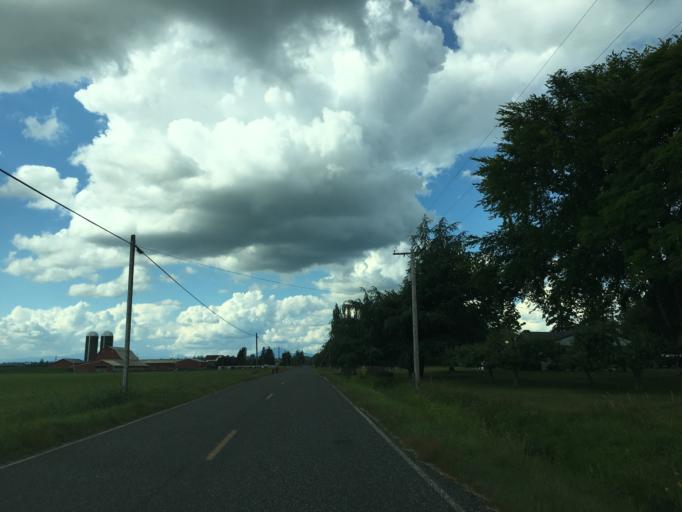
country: US
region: Washington
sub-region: Whatcom County
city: Lynden
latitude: 48.9697
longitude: -122.4739
